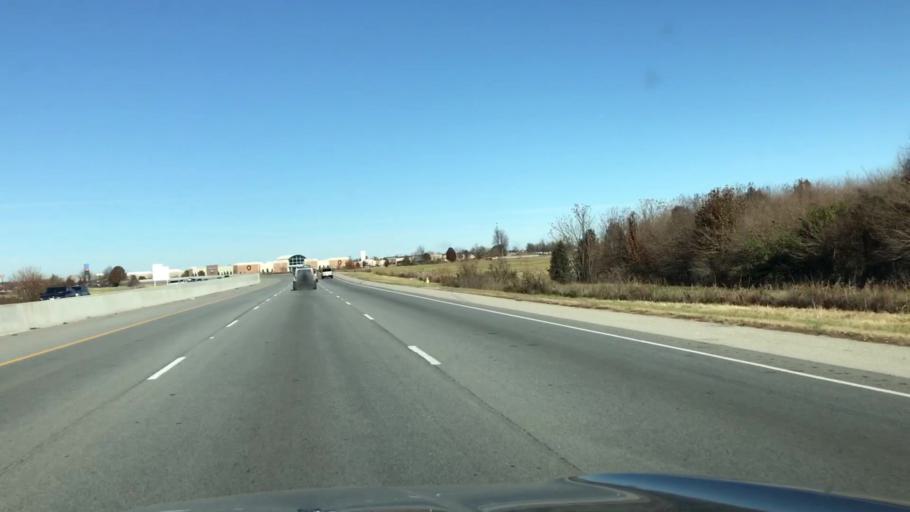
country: US
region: Arkansas
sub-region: Benton County
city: Lowell
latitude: 36.2711
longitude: -94.1499
